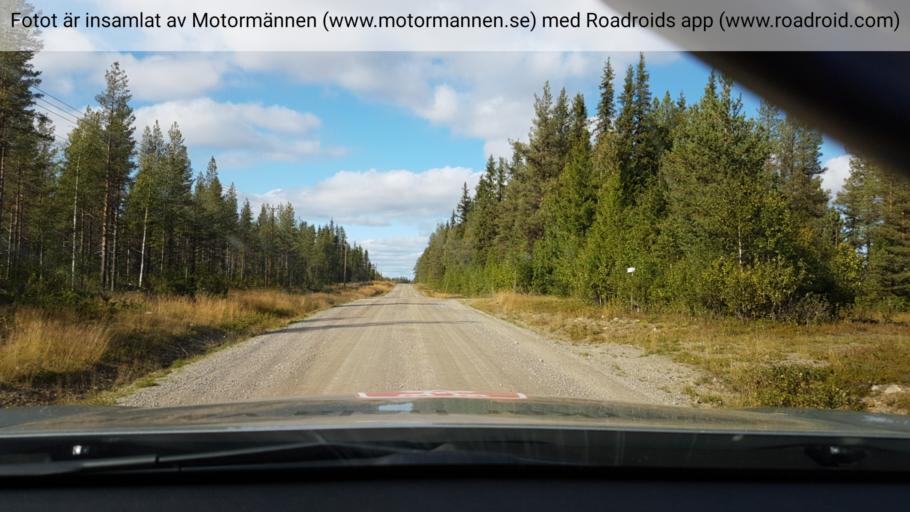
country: SE
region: Vaesterbotten
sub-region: Sorsele Kommun
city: Sorsele
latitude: 65.4786
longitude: 18.1114
